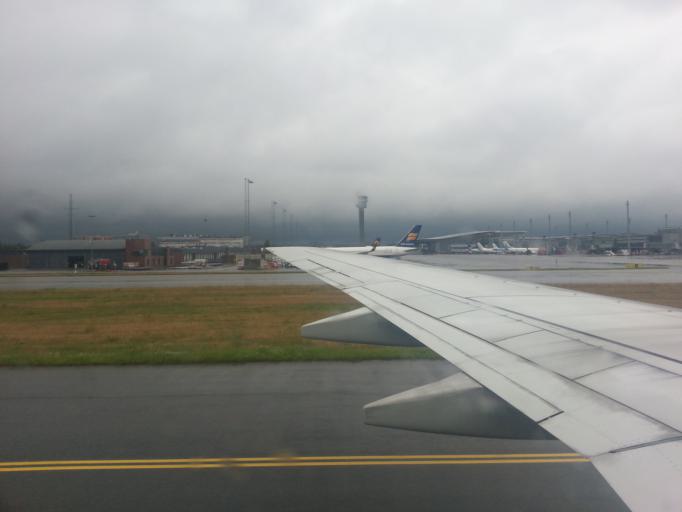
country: NO
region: Akershus
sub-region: Ullensaker
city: Jessheim
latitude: 60.1902
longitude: 11.1116
